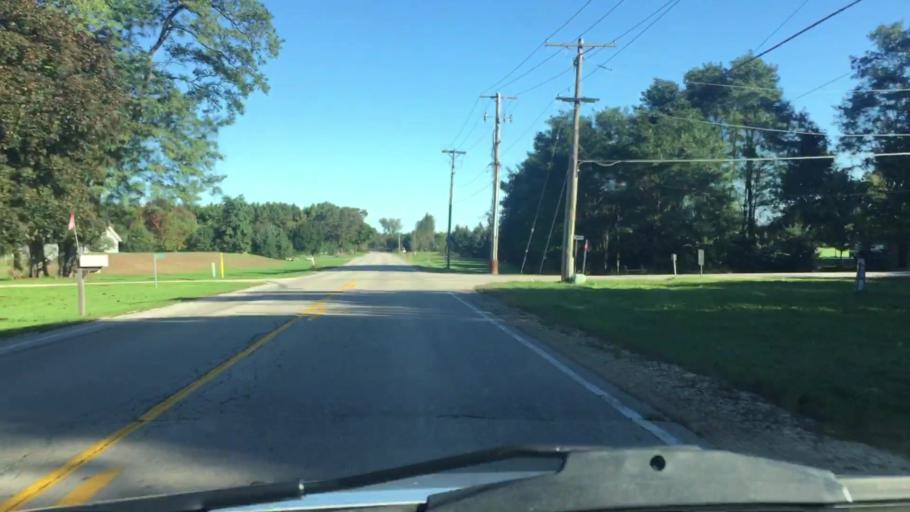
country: US
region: Wisconsin
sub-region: Waukesha County
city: North Prairie
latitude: 42.9591
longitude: -88.4049
